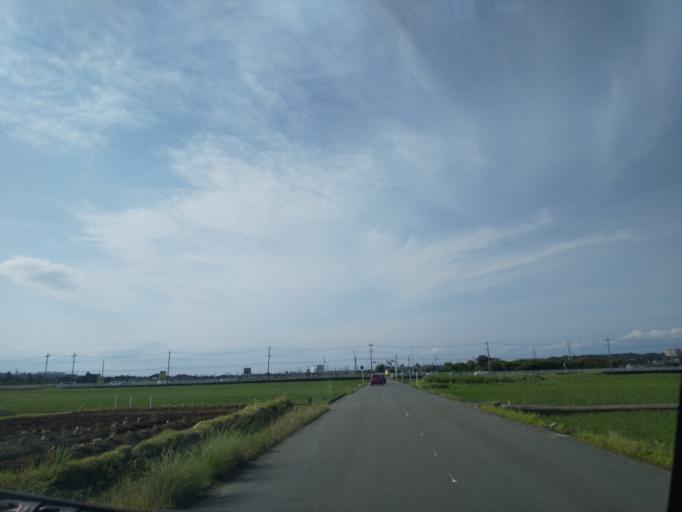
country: JP
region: Kanagawa
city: Zama
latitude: 35.4848
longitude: 139.3818
